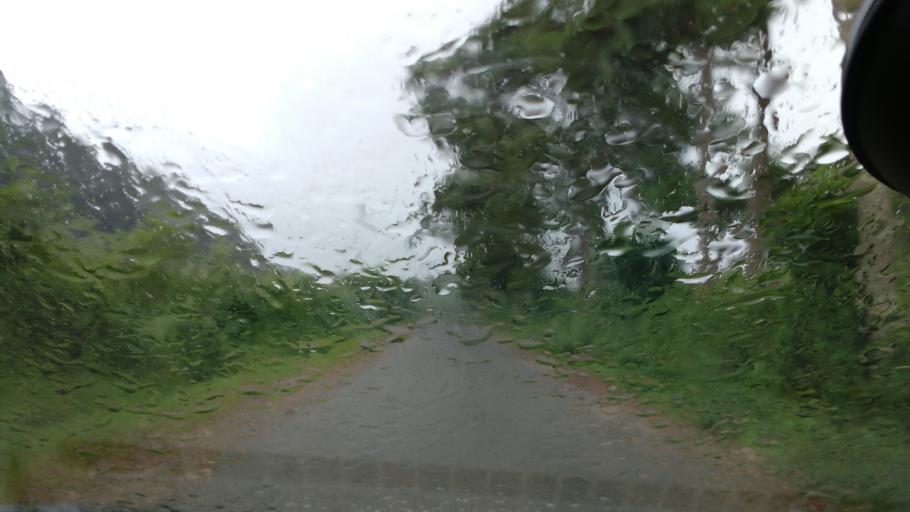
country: IN
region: Meghalaya
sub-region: East Khasi Hills
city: Shillong
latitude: 25.5438
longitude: 91.8470
